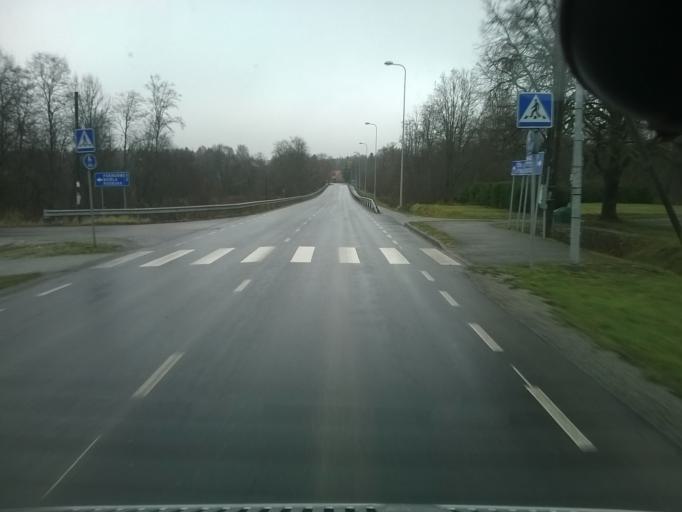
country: EE
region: Harju
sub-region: Saku vald
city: Saku
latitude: 59.2319
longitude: 24.6806
